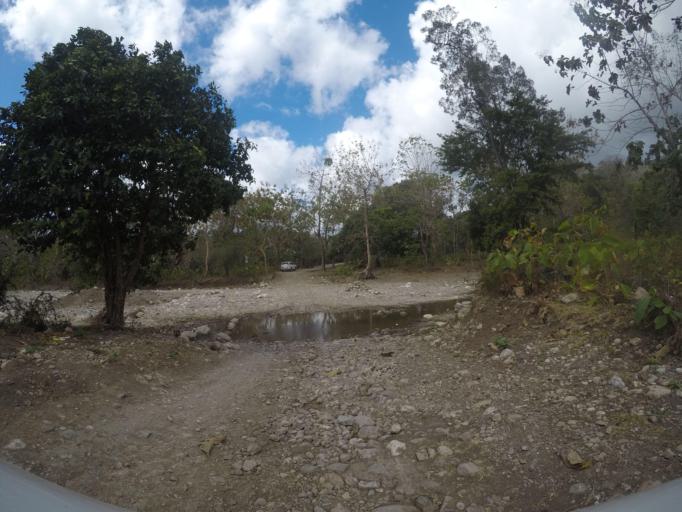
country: TL
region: Lautem
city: Lospalos
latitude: -8.5199
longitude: 126.8416
